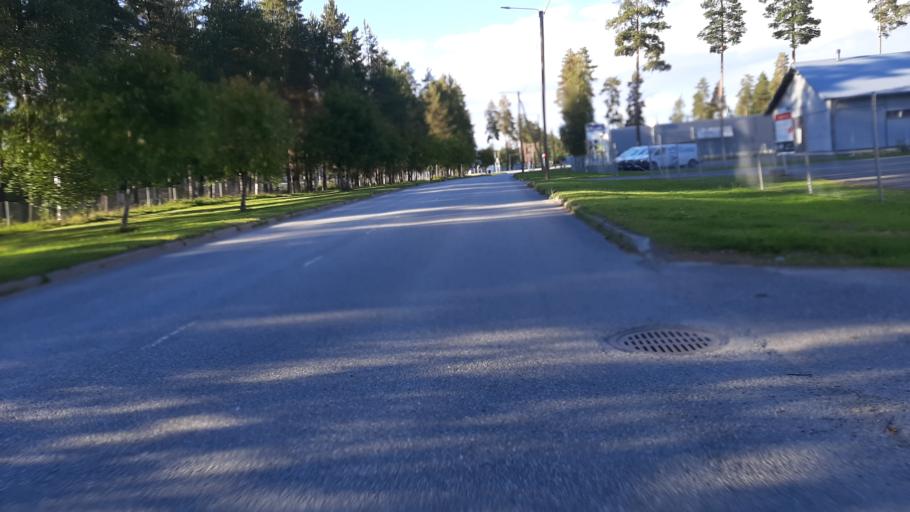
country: FI
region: North Karelia
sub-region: Joensuu
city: Joensuu
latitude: 62.6262
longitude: 29.7712
